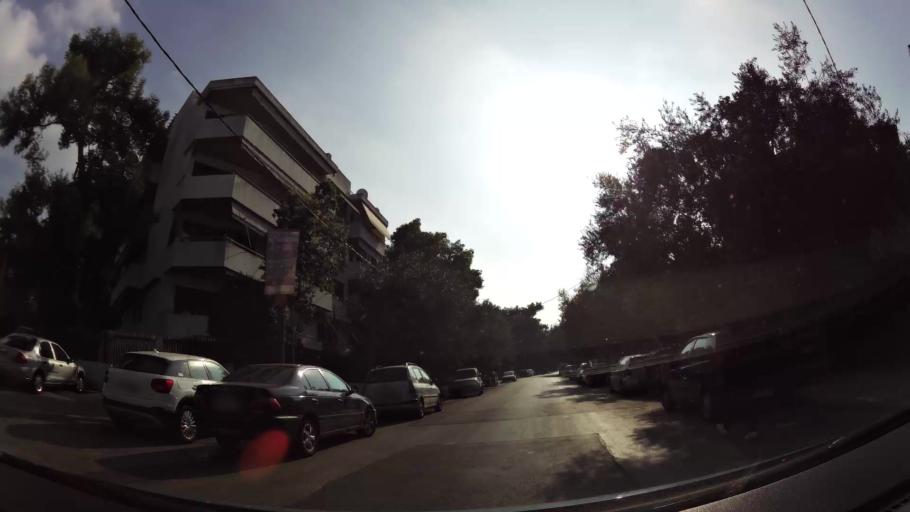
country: GR
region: Attica
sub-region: Nomarchia Athinas
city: Agia Paraskevi
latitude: 38.0048
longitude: 23.8187
